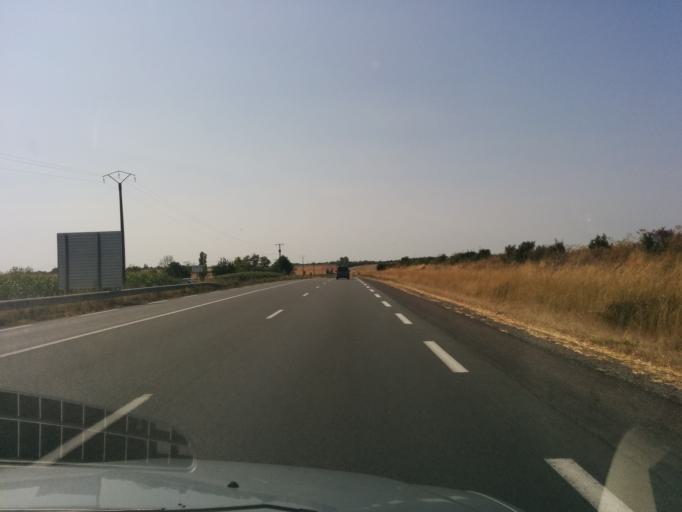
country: FR
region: Poitou-Charentes
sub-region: Departement de la Vienne
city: Neuville-de-Poitou
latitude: 46.6957
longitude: 0.2499
